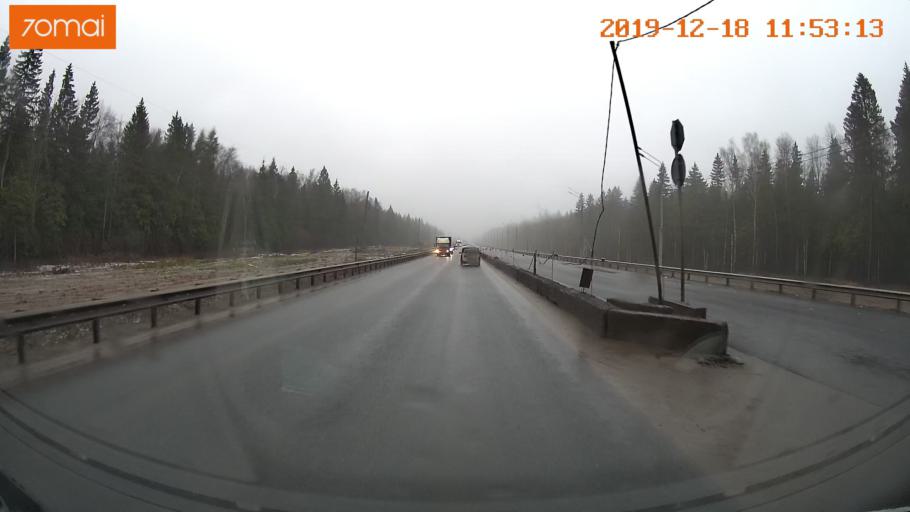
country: RU
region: Moskovskaya
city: Yershovo
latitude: 55.8022
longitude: 36.9205
